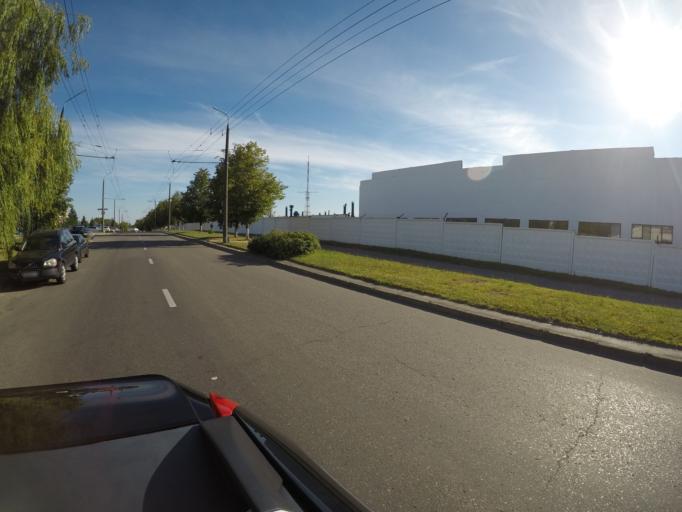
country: BY
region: Grodnenskaya
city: Hrodna
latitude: 53.7103
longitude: 23.8270
